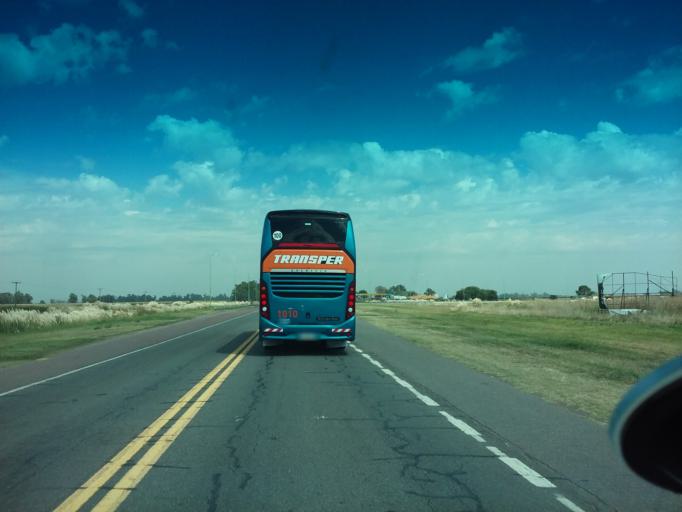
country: AR
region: Buenos Aires
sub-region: Partido de Carlos Casares
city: Carlos Casares
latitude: -35.6554
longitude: -61.3951
